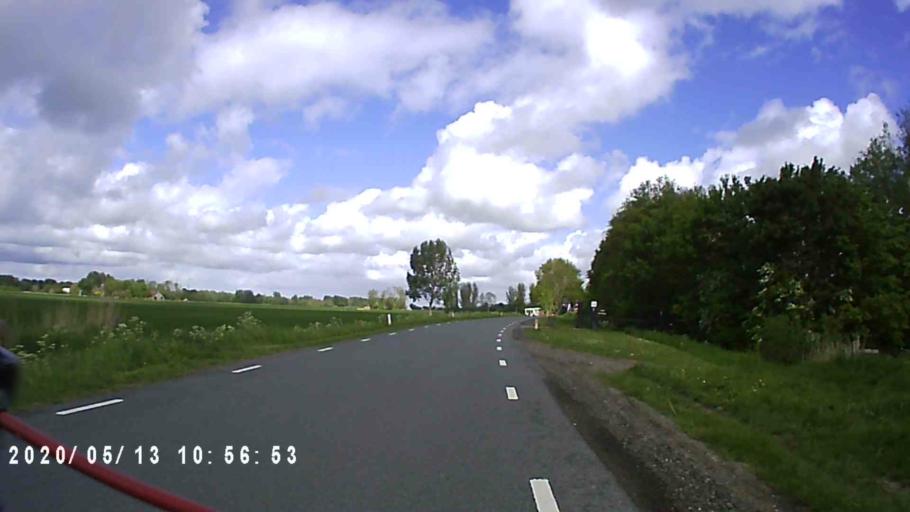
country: NL
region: Groningen
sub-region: Gemeente Zuidhorn
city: Grijpskerk
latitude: 53.2713
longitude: 6.3347
